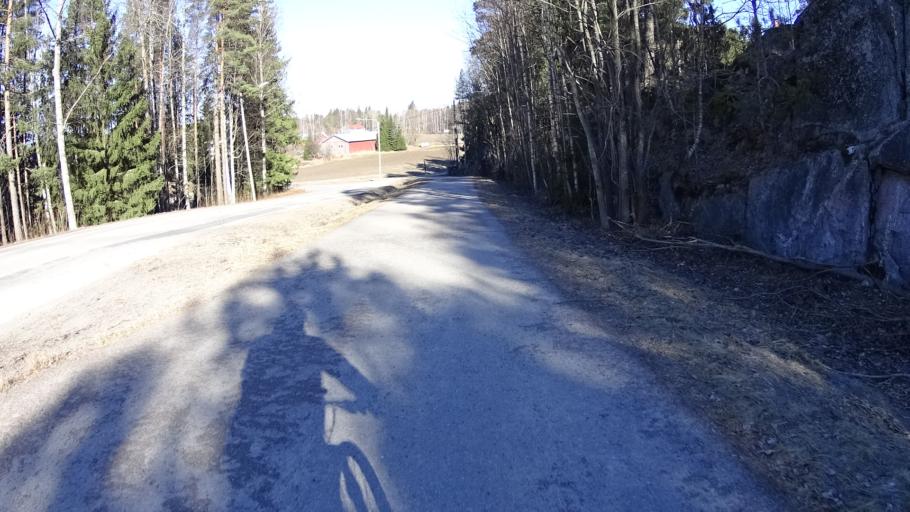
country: FI
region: Uusimaa
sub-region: Helsinki
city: Espoo
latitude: 60.2290
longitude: 24.6652
